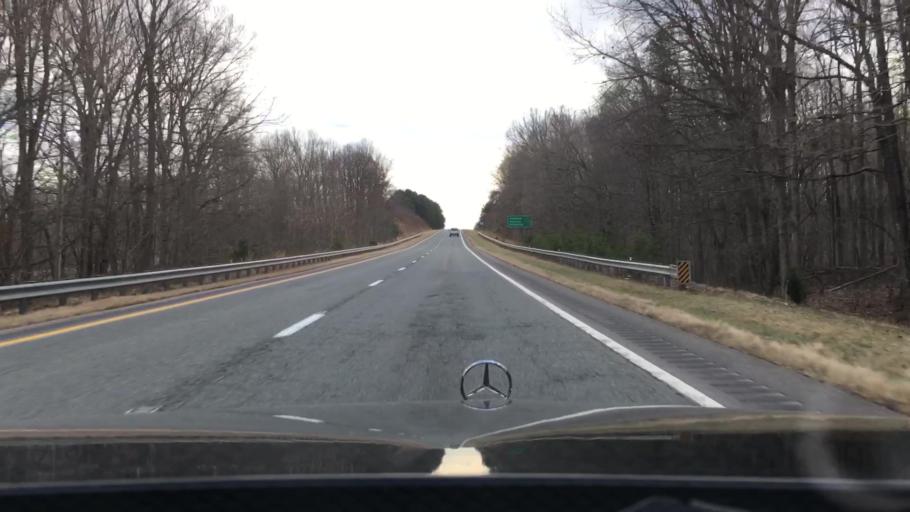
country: US
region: Virginia
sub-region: Pittsylvania County
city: Gretna
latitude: 36.9421
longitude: -79.3777
